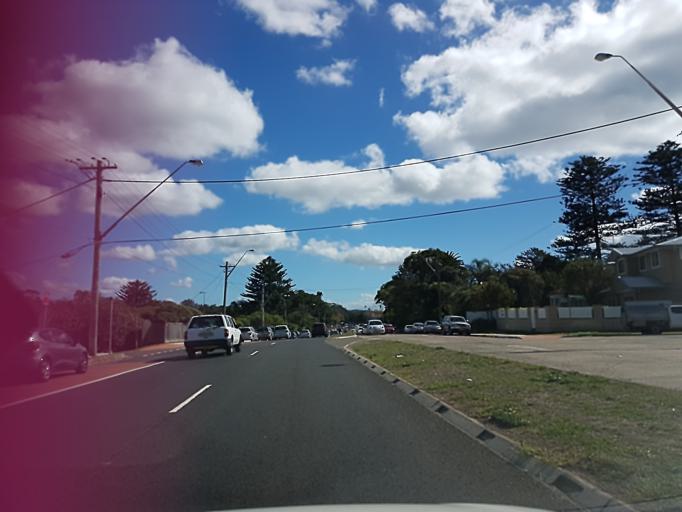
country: AU
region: New South Wales
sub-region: Warringah
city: Narrabeen
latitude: -33.7170
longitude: 151.2975
